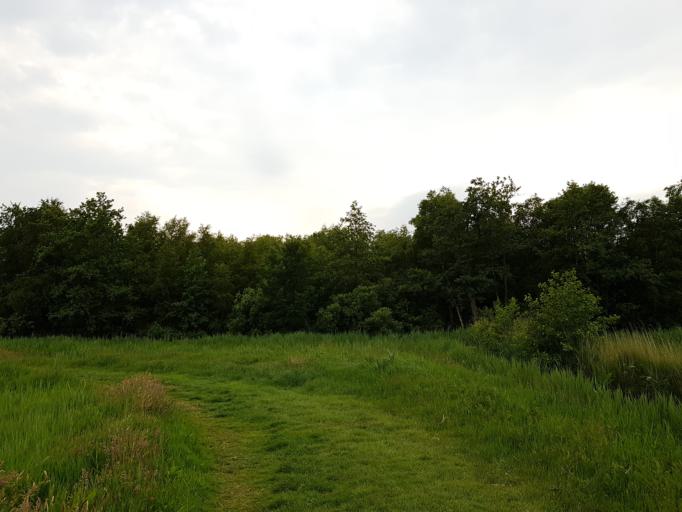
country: NL
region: Friesland
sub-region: Gemeente Tytsjerksteradiel
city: Garyp
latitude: 53.1406
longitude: 5.9386
